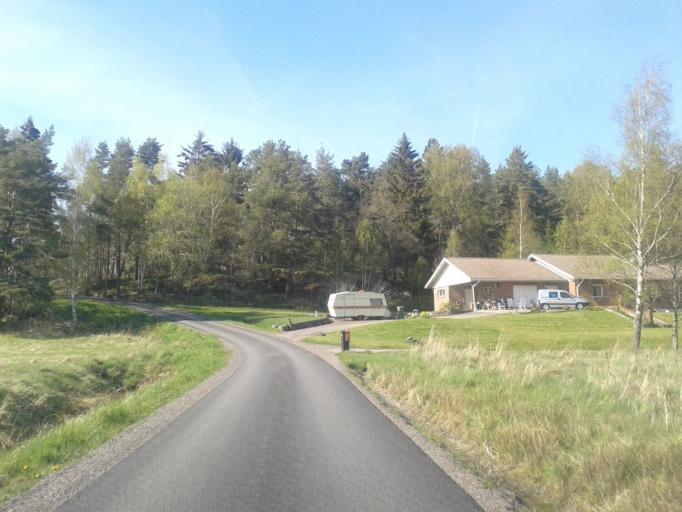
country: SE
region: Vaestra Goetaland
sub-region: Ale Kommun
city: Alafors
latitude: 57.8931
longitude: 12.0828
